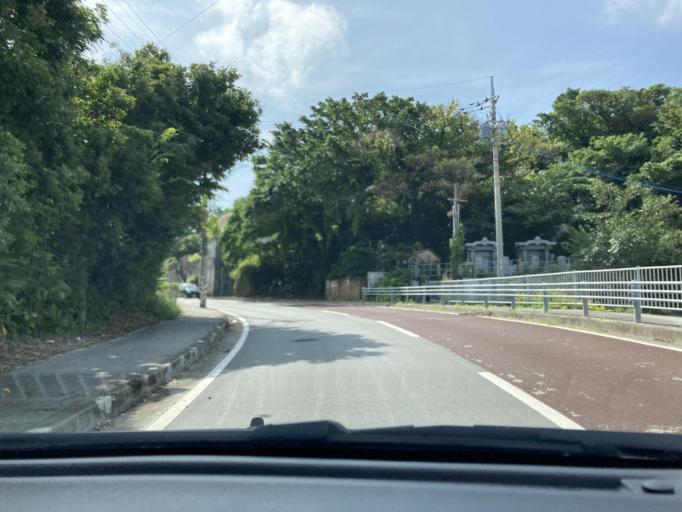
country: JP
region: Okinawa
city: Chatan
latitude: 26.2943
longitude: 127.7954
